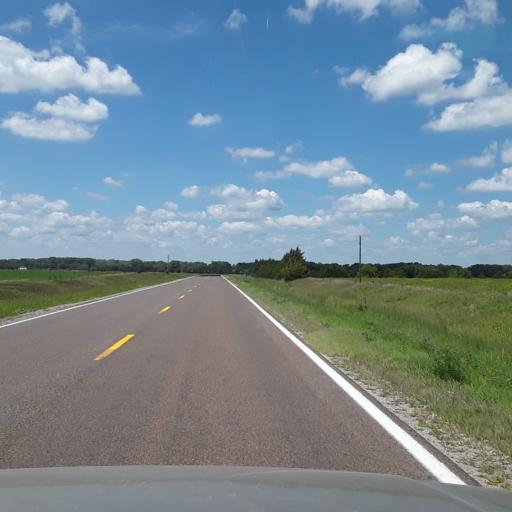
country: US
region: Nebraska
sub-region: Nance County
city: Genoa
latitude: 41.4058
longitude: -97.7107
